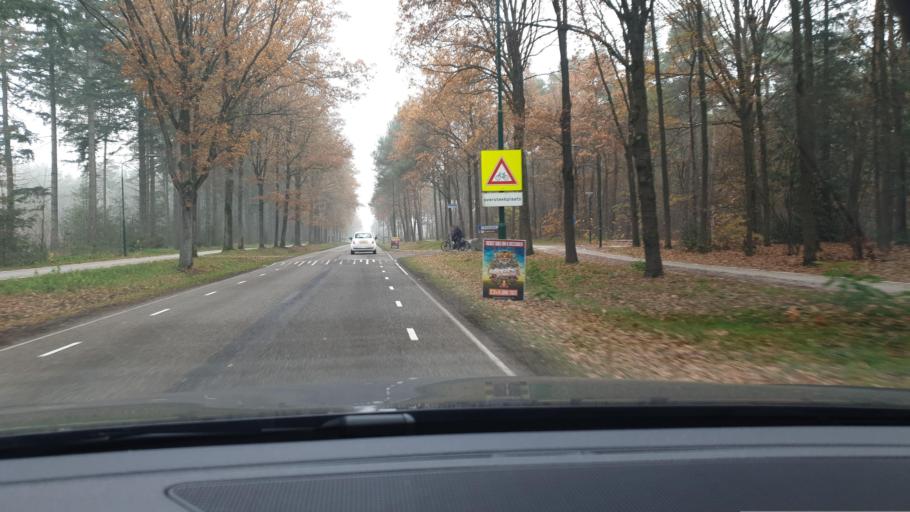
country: NL
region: North Brabant
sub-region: Bergeijk
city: Bergeyk
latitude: 51.3316
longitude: 5.3513
